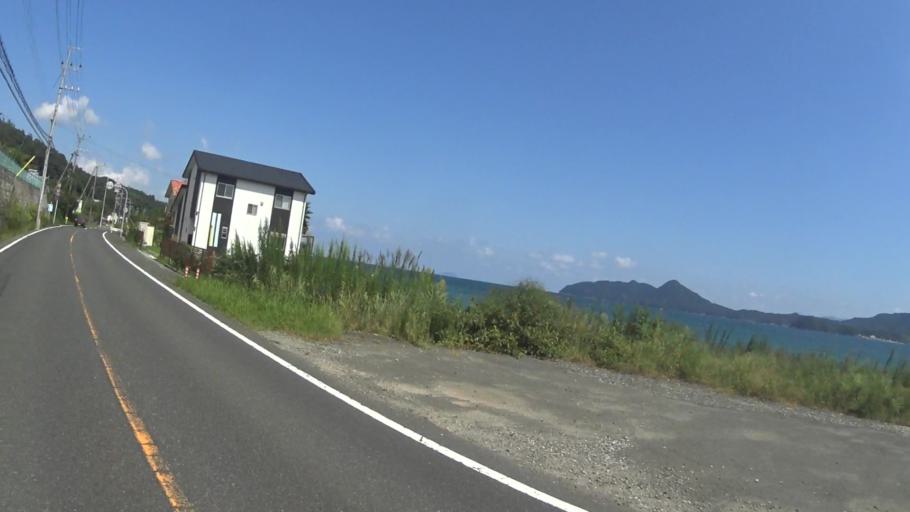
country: JP
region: Kyoto
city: Miyazu
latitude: 35.5886
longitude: 135.2071
